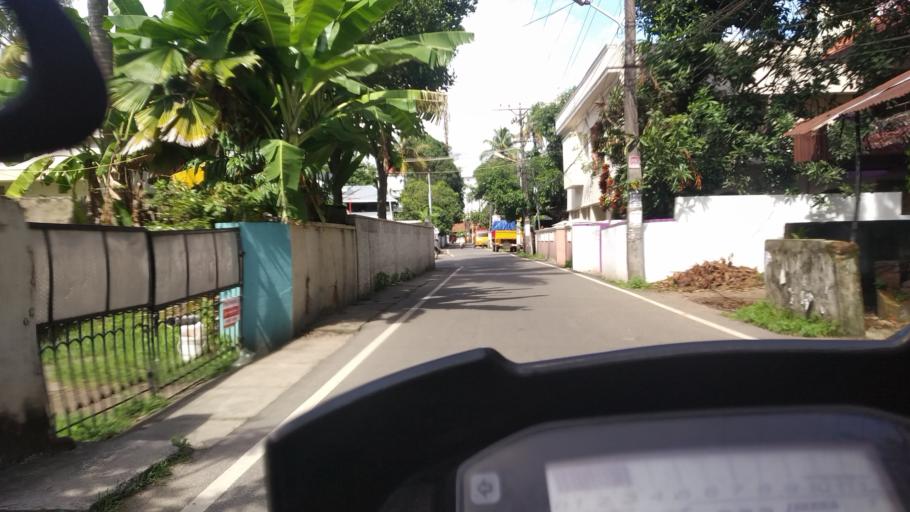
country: IN
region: Kerala
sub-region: Ernakulam
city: Elur
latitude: 10.0227
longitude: 76.2726
